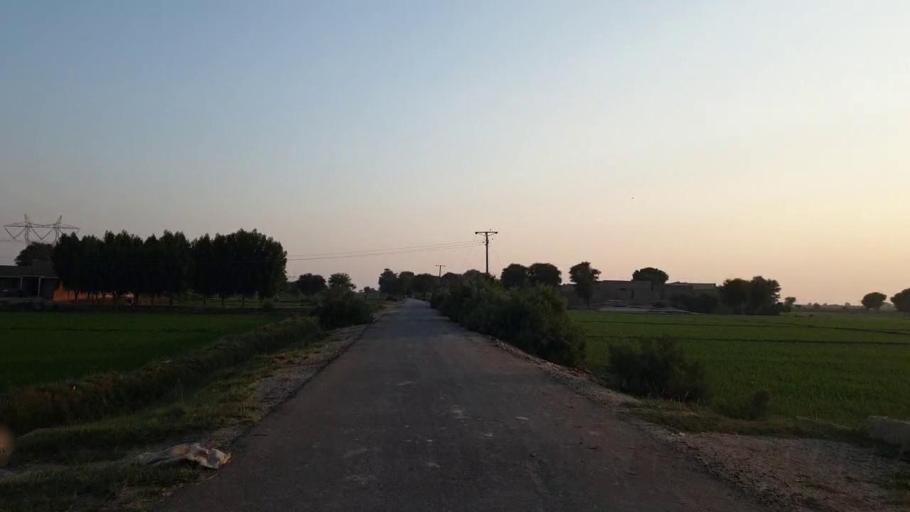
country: PK
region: Sindh
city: Sehwan
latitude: 26.4445
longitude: 67.7618
